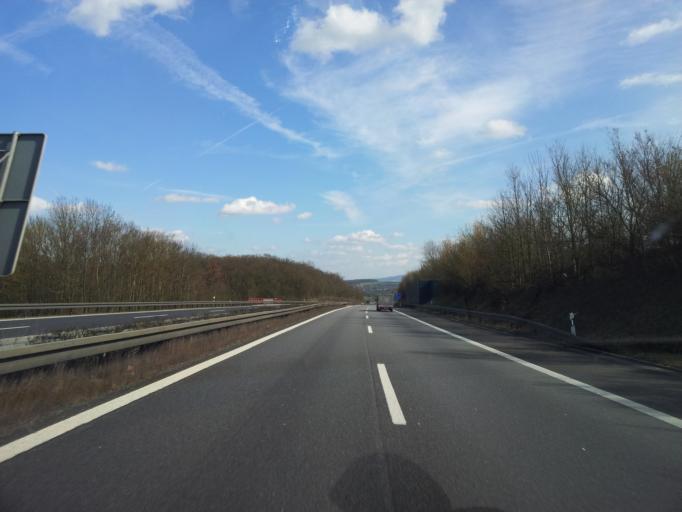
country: DE
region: Bavaria
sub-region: Regierungsbezirk Unterfranken
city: Schonungen
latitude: 50.0271
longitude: 10.3089
